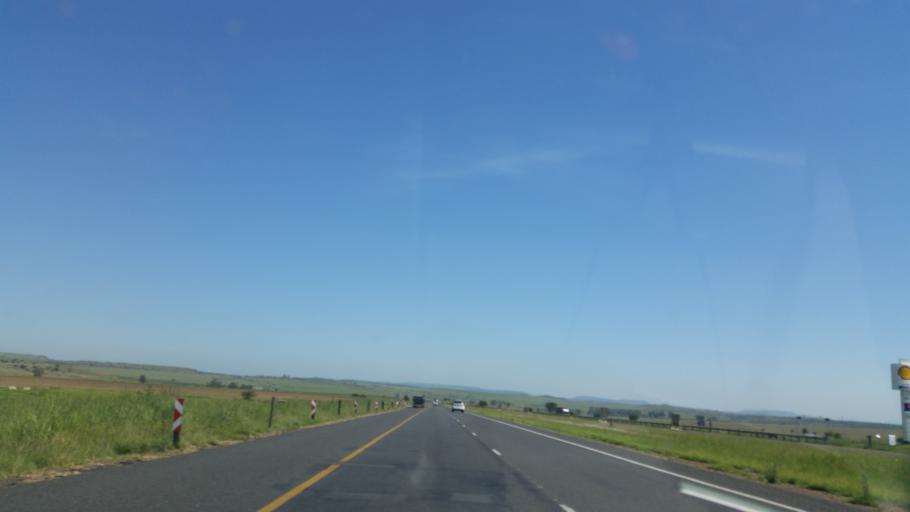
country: ZA
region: KwaZulu-Natal
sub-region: uThukela District Municipality
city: Estcourt
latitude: -28.9231
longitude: 29.7801
